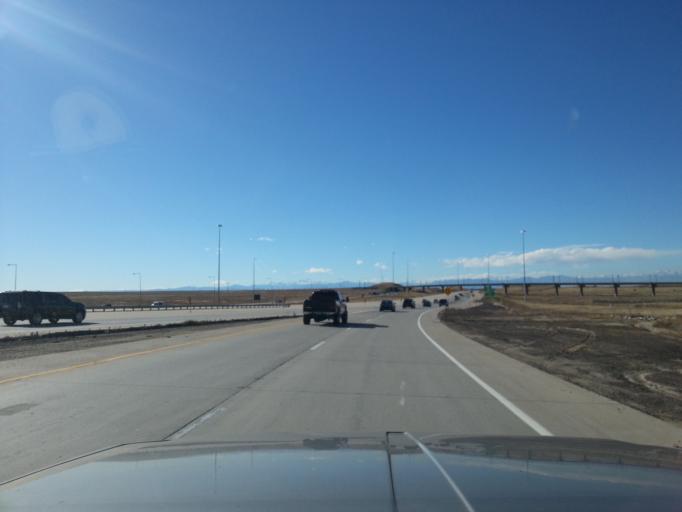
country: US
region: Colorado
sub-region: Adams County
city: Aurora
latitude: 39.8347
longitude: -104.7261
